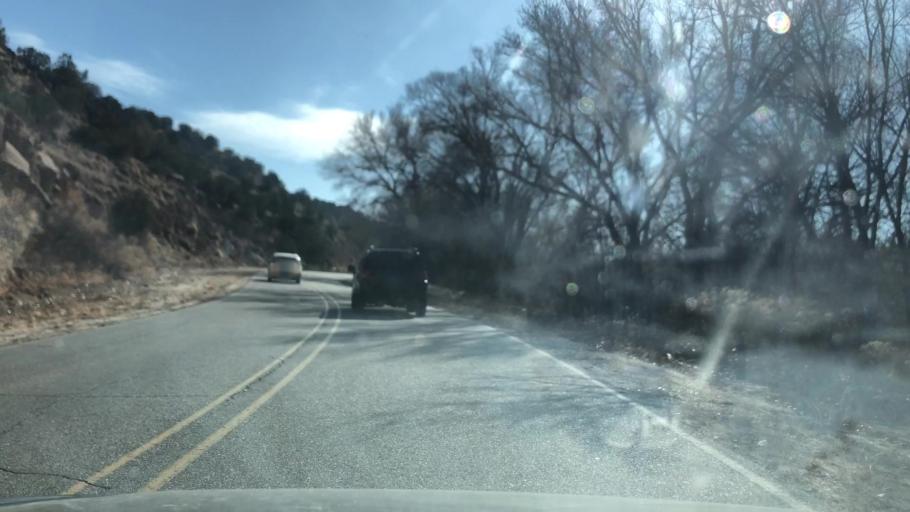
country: US
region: New Mexico
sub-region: Rio Arriba County
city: Ohkay Owingeh
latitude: 36.0887
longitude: -106.1291
